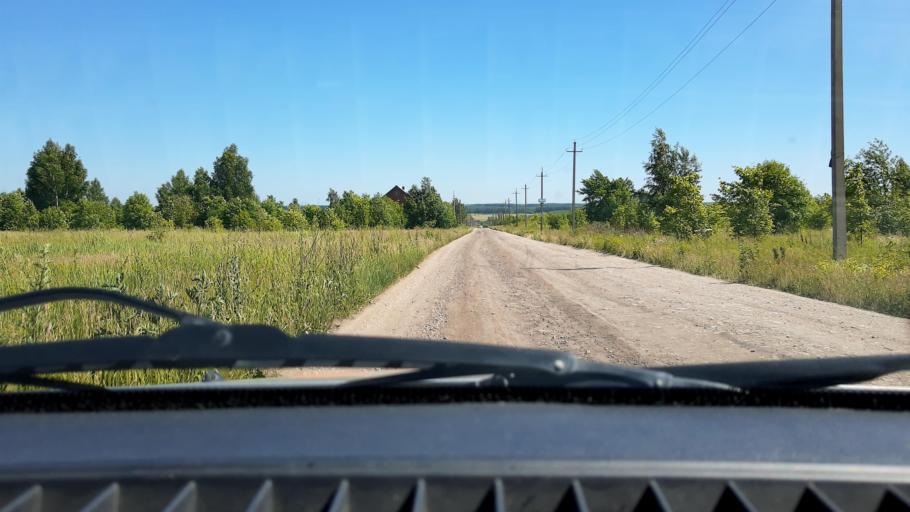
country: RU
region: Bashkortostan
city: Avdon
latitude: 54.5525
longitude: 55.7066
